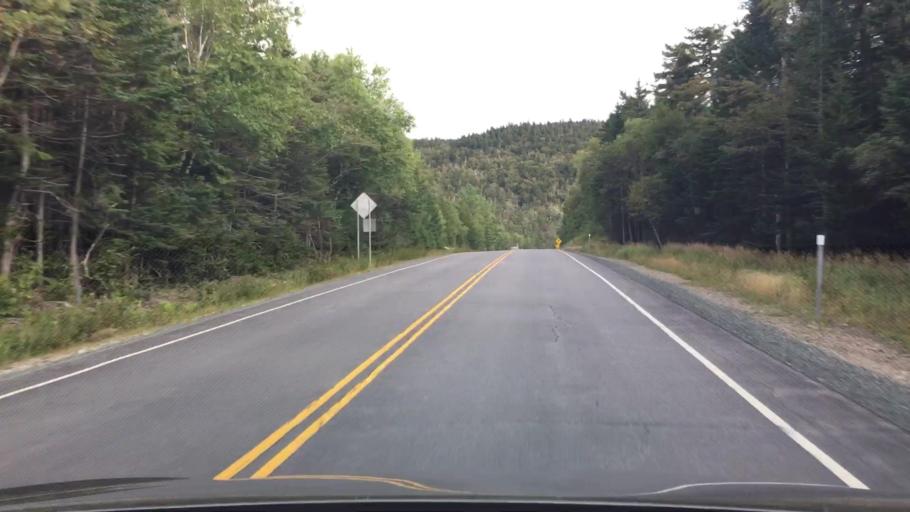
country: US
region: New Hampshire
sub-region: Grafton County
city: Woodstock
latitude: 44.0370
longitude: -71.4996
